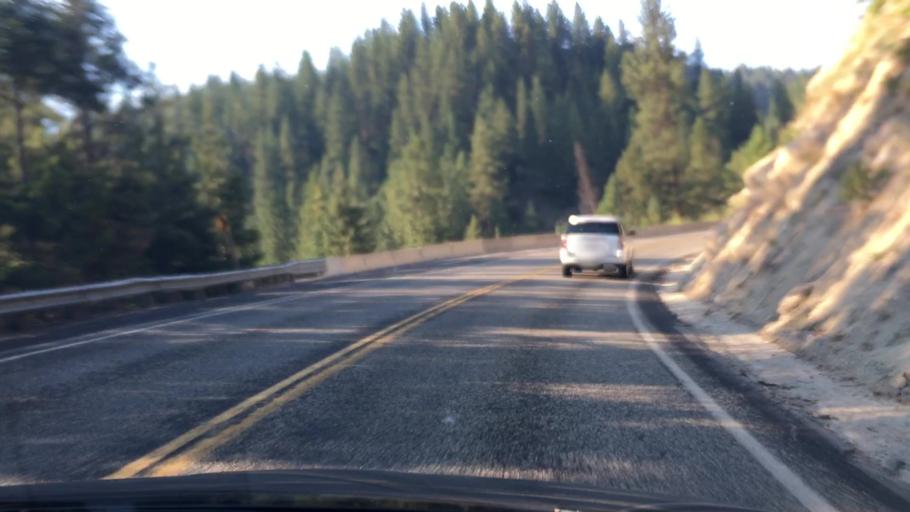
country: US
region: Idaho
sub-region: Valley County
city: Cascade
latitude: 44.3285
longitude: -116.0583
